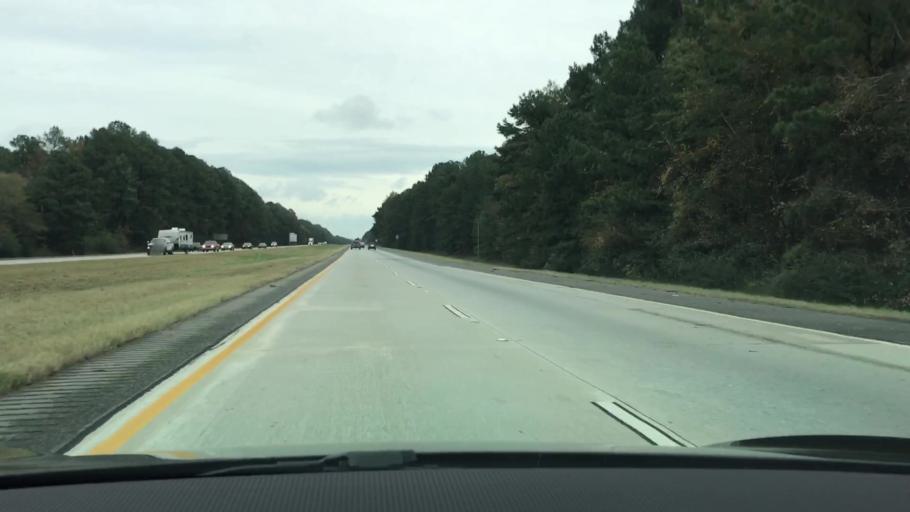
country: US
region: Georgia
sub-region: Greene County
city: Union Point
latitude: 33.5451
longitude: -83.0727
